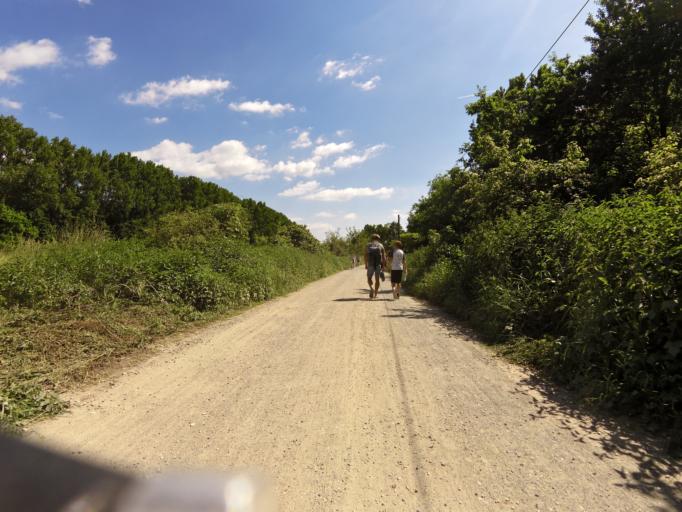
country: DE
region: Rheinland-Pfalz
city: Nackenheim
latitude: 49.9281
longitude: 8.3522
